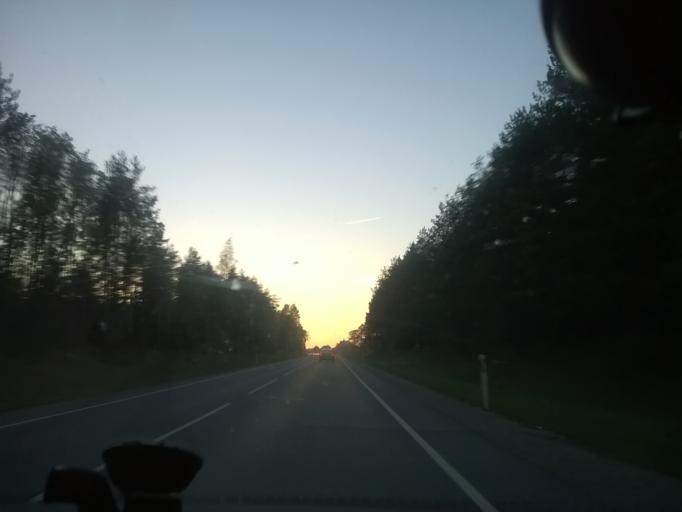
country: EE
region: Laeaene
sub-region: Lihula vald
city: Lihula
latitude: 58.9735
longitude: 23.9119
